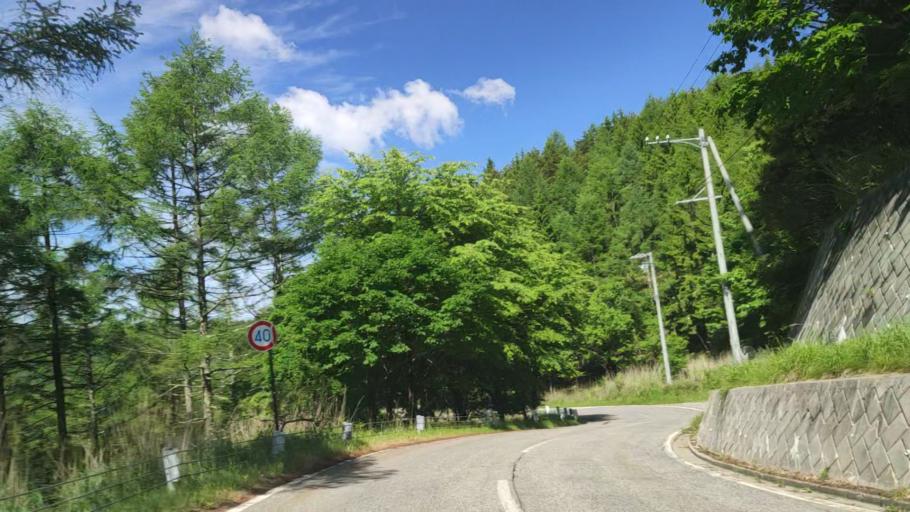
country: JP
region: Nagano
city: Suwa
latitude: 36.0985
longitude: 138.1453
